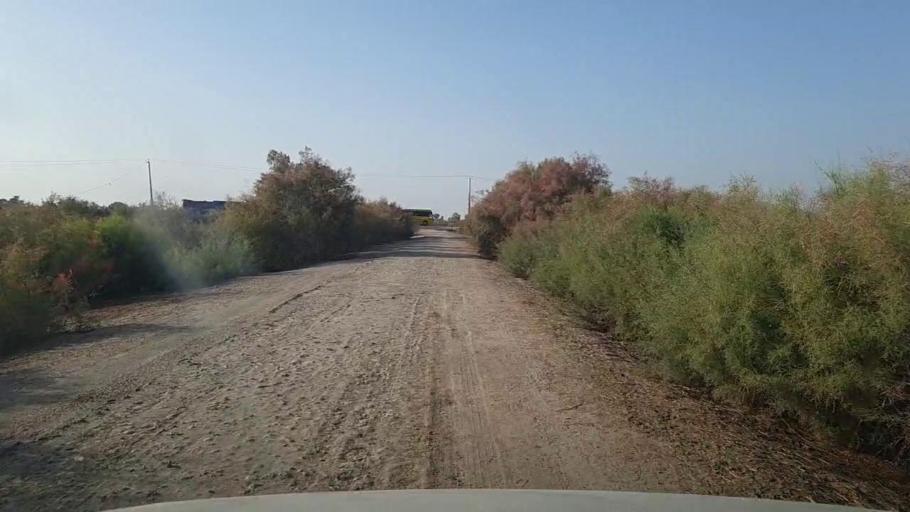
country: PK
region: Sindh
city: Kandhkot
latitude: 28.3105
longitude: 69.3274
